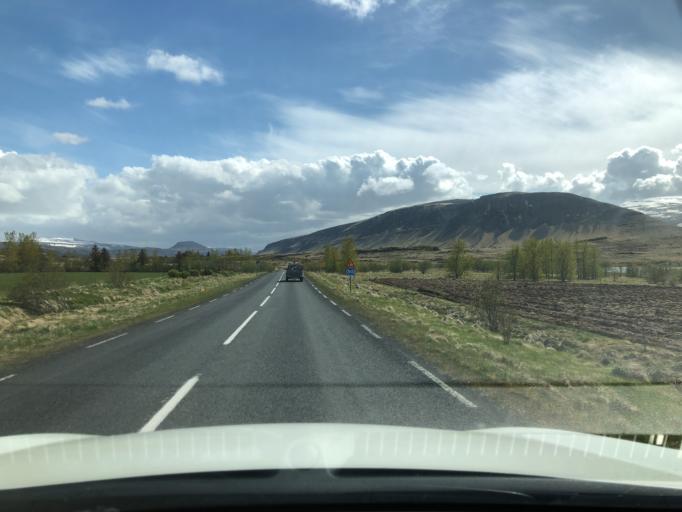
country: IS
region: Capital Region
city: Mosfellsbaer
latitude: 64.3444
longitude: -21.6139
